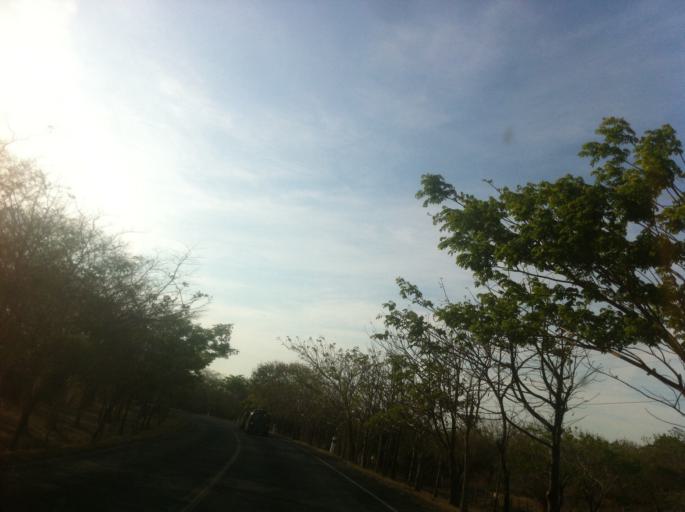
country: NI
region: Rivas
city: Cardenas
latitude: 11.2710
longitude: -85.6504
